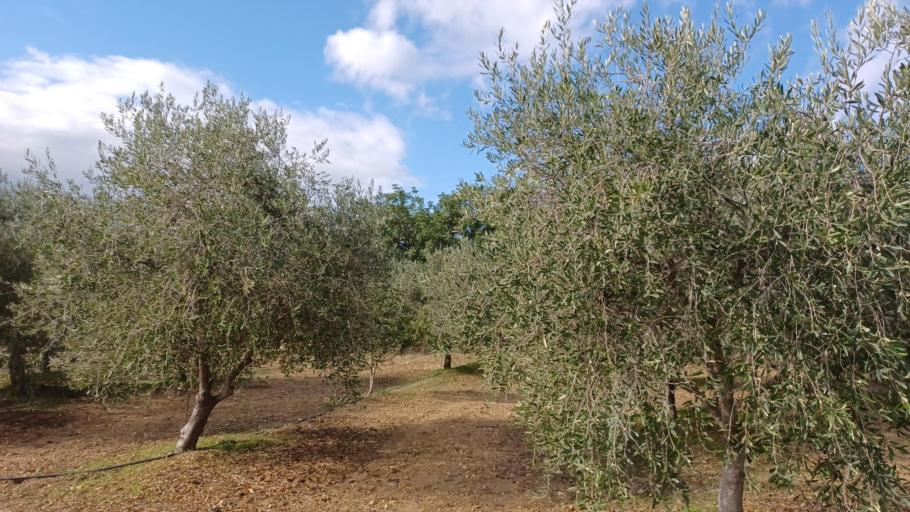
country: CY
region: Limassol
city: Sotira
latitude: 34.7440
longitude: 32.8575
